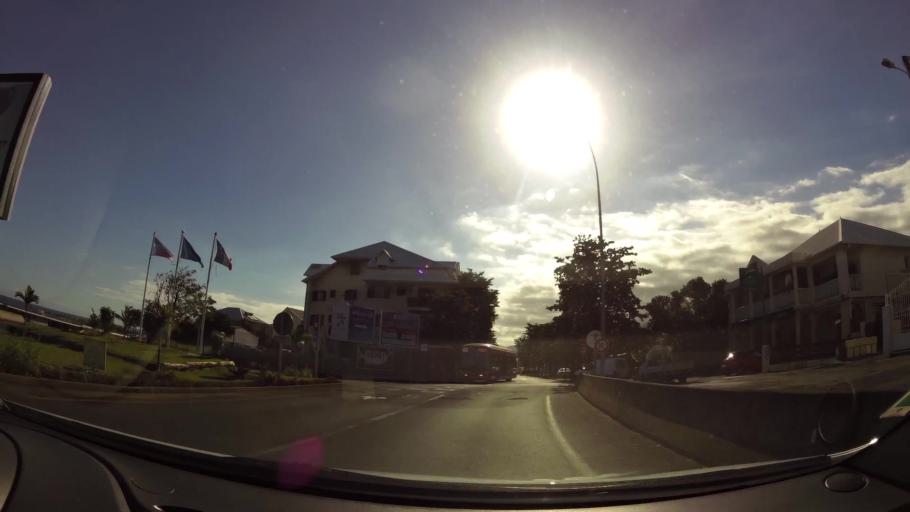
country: RE
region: Reunion
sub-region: Reunion
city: Saint-Louis
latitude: -21.2915
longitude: 55.4145
